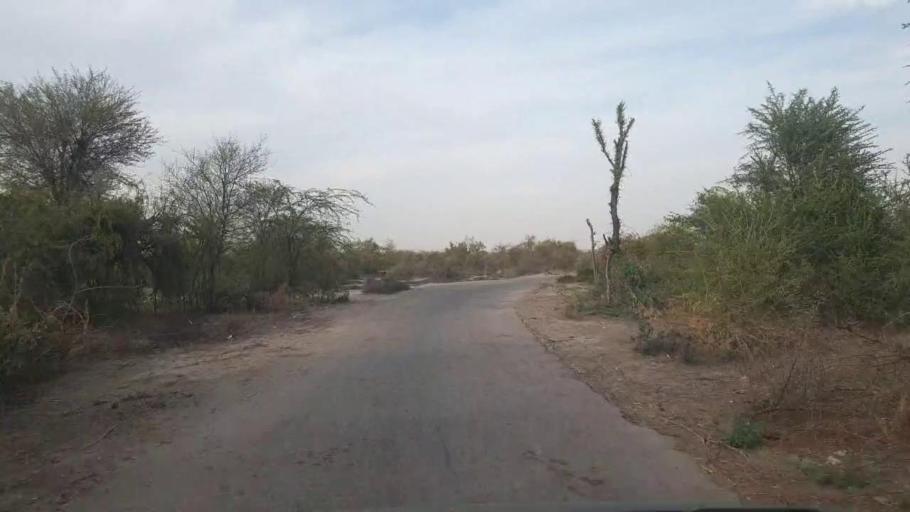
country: PK
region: Sindh
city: Nabisar
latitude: 25.1112
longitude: 69.6780
